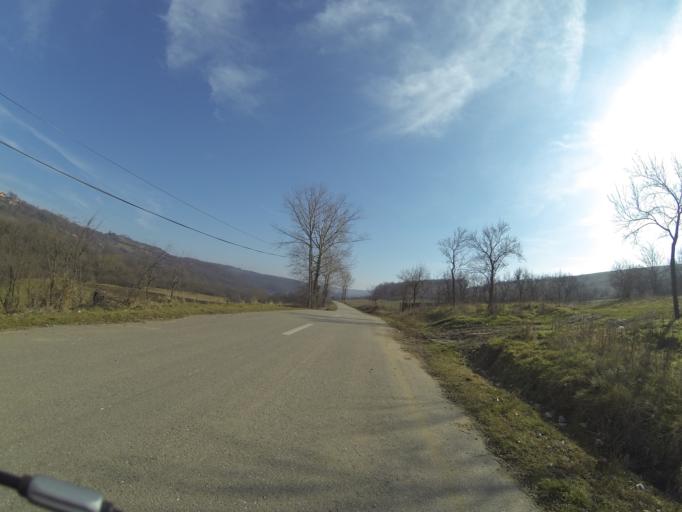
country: RO
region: Mehedinti
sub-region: Comuna Poroina Mare
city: Poroina Mare
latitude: 44.4944
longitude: 22.9286
